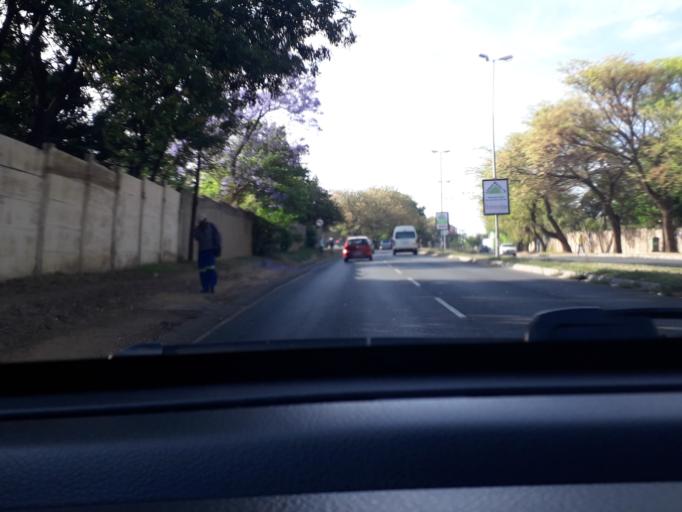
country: ZA
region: Gauteng
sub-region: City of Johannesburg Metropolitan Municipality
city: Modderfontein
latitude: -26.0680
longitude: 28.0763
